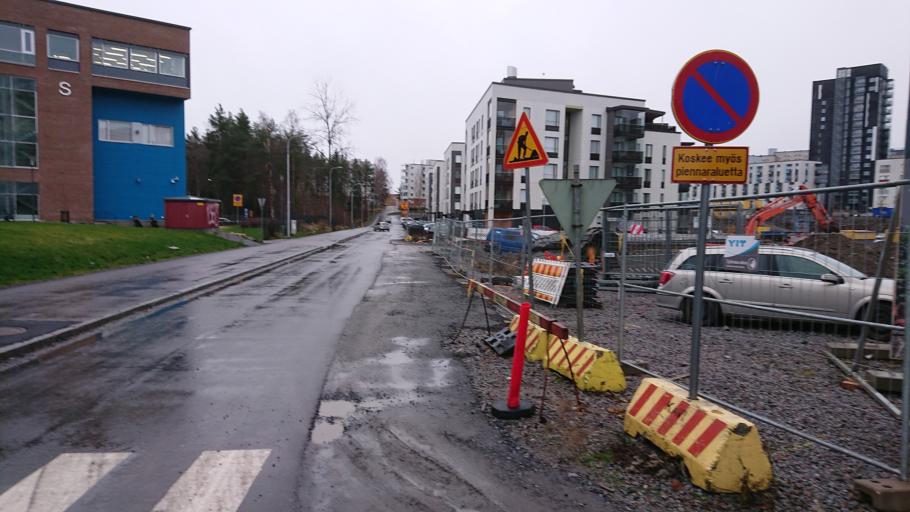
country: FI
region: Pirkanmaa
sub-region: Tampere
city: Tampere
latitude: 61.4575
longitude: 23.8525
